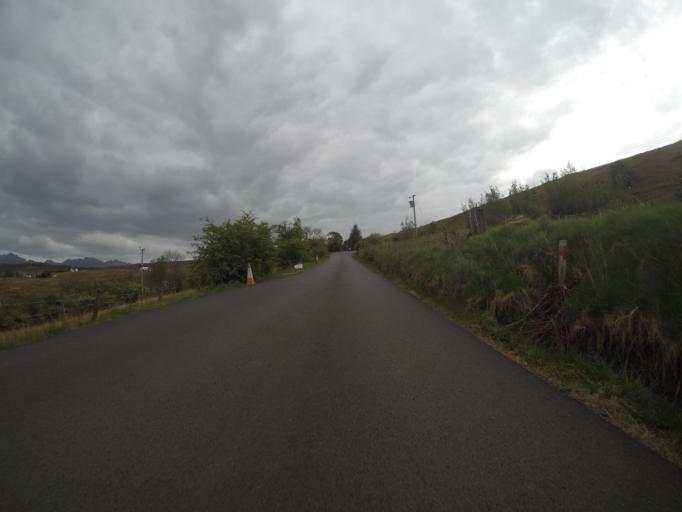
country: GB
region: Scotland
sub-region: Highland
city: Isle of Skye
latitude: 57.3010
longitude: -6.3578
